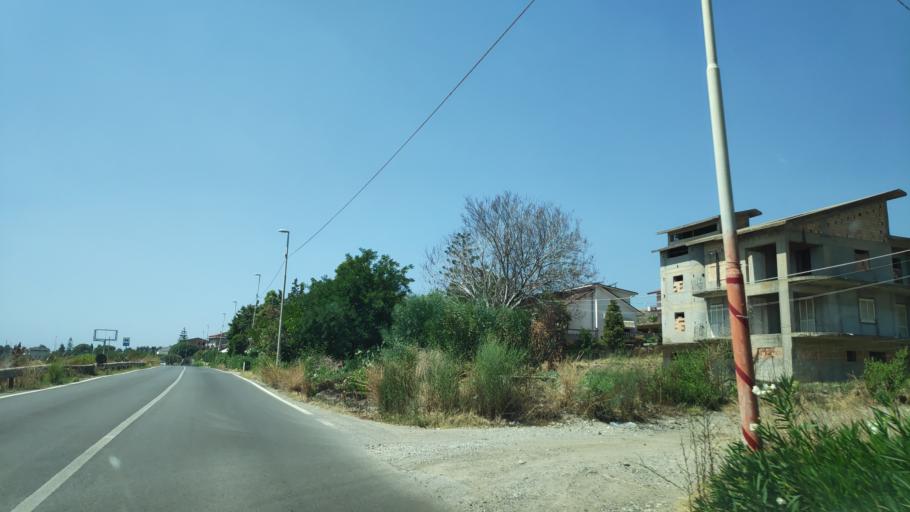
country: IT
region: Calabria
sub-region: Provincia di Reggio Calabria
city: Weather Station
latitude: 37.9533
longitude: 16.0909
